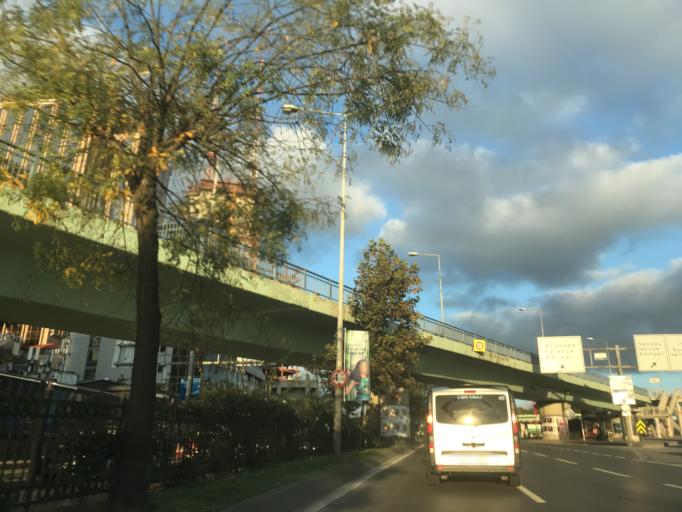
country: TR
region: Istanbul
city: Sisli
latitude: 41.1084
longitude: 29.0214
